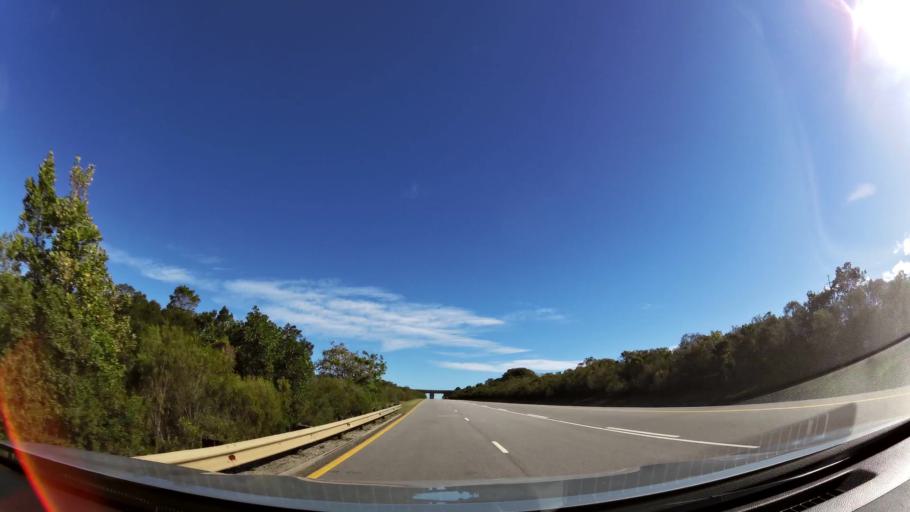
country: ZA
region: Eastern Cape
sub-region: Cacadu District Municipality
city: Kruisfontein
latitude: -34.0173
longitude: 24.6240
